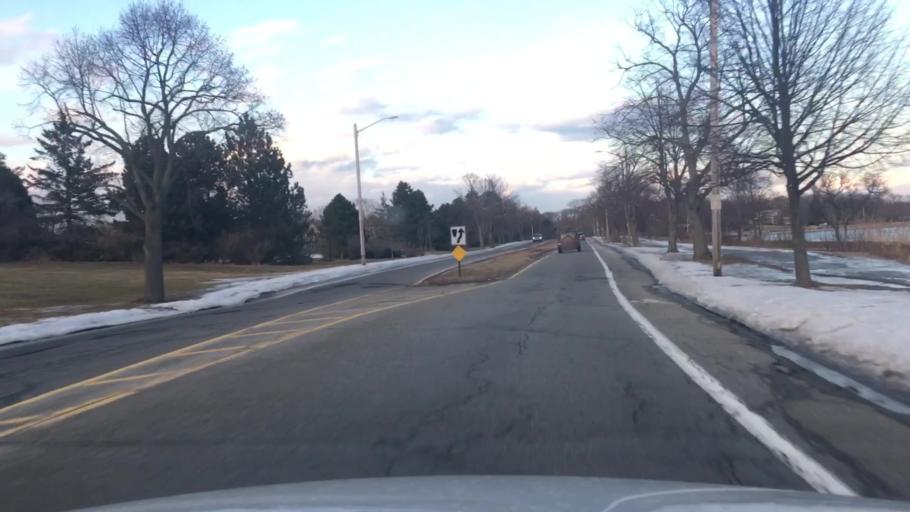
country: US
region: Maine
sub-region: Cumberland County
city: Portland
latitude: 43.6771
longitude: -70.2753
